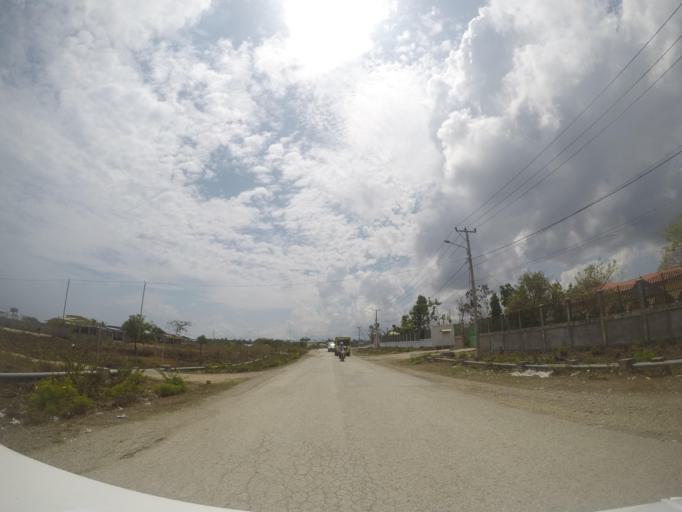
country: TL
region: Baucau
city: Baucau
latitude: -8.4732
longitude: 126.4435
